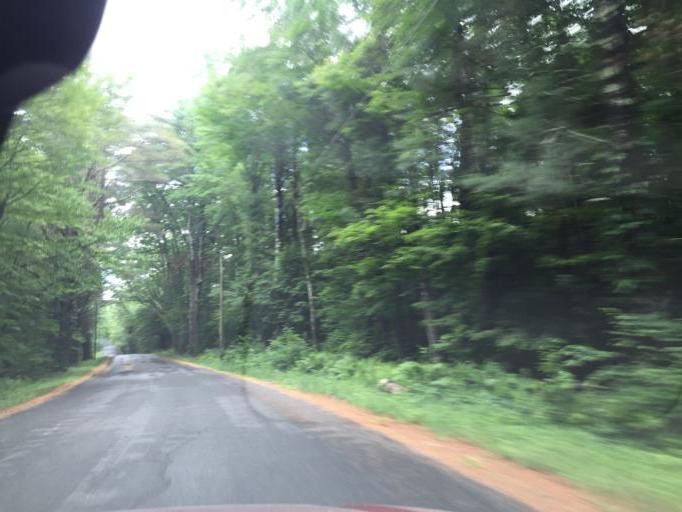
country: US
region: Connecticut
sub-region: Litchfield County
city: Litchfield
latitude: 41.7874
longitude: -73.2594
